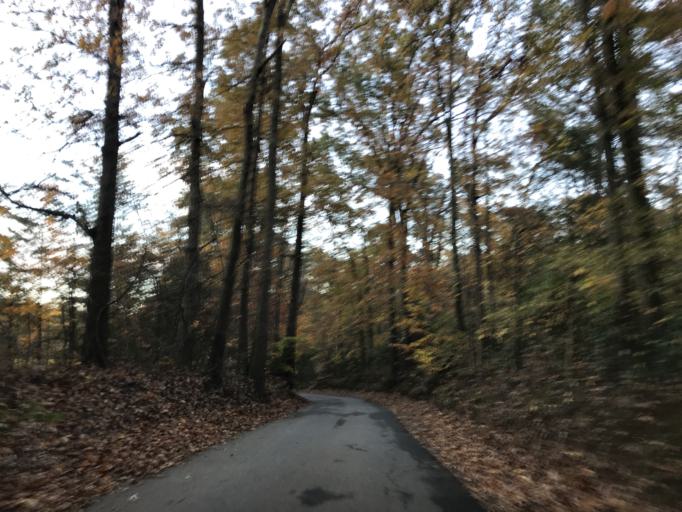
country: US
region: Maryland
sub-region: Baltimore County
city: White Marsh
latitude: 39.3716
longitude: -76.3998
